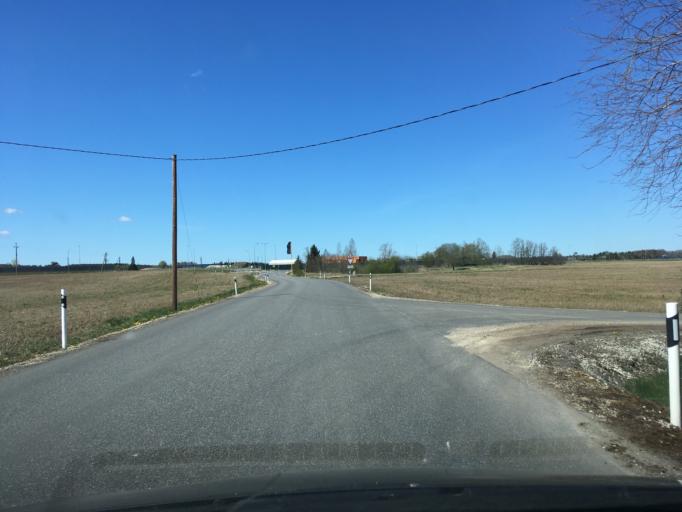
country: EE
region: Harju
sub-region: Rae vald
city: Vaida
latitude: 59.1980
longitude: 25.0473
